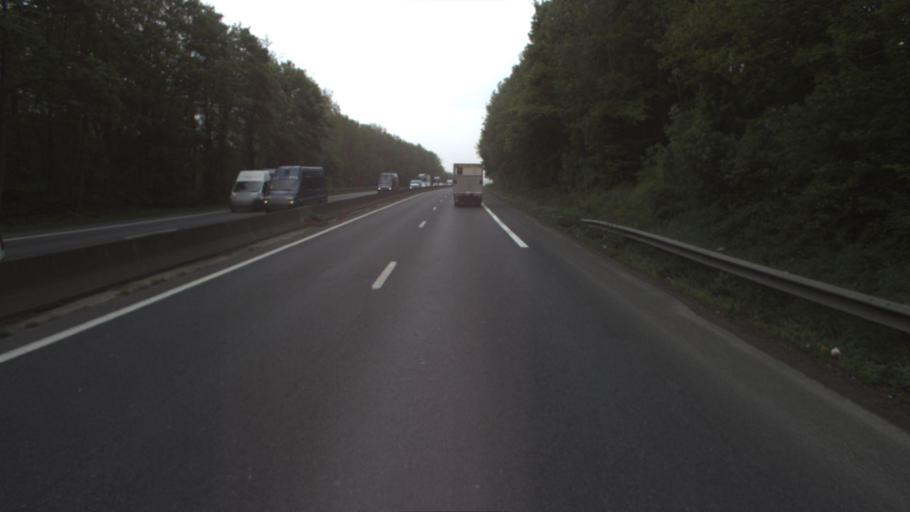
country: FR
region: Ile-de-France
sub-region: Departement de Seine-et-Marne
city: Saint-Mard
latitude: 49.0474
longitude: 2.6934
